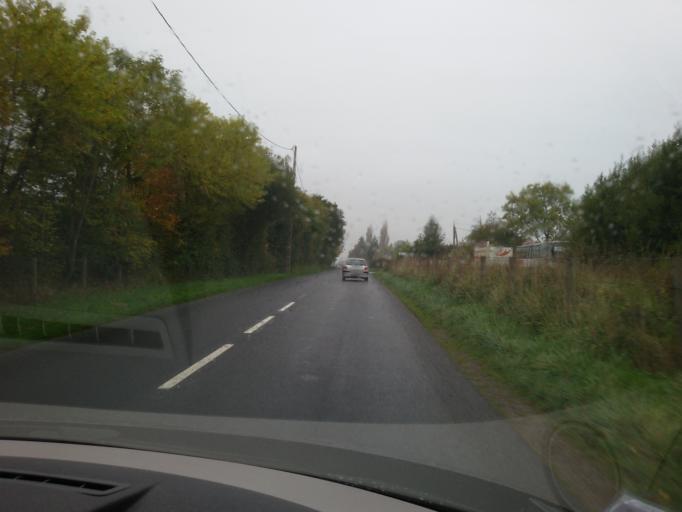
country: FR
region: Lower Normandy
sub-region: Departement du Calvados
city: Villers-sur-Mer
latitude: 49.3086
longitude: -0.0201
